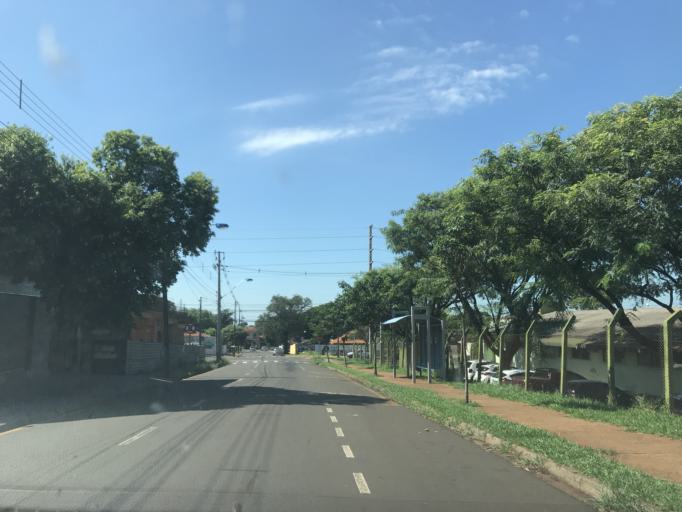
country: BR
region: Parana
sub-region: Maringa
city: Maringa
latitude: -23.4493
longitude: -51.9593
